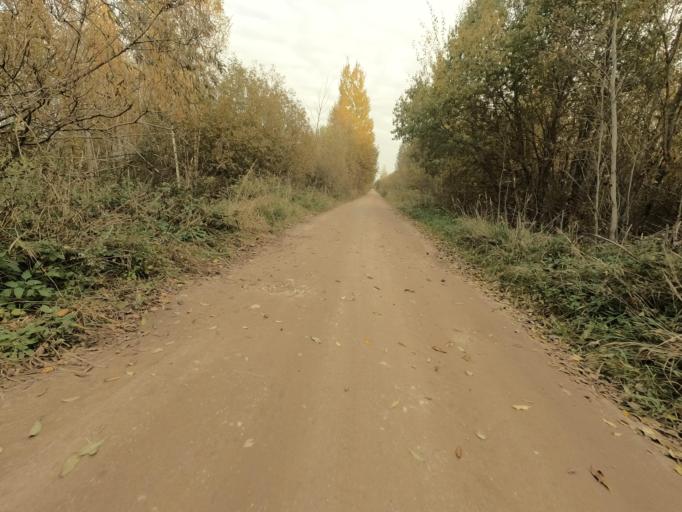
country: RU
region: Novgorod
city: Pankovka
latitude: 58.8975
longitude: 30.9979
